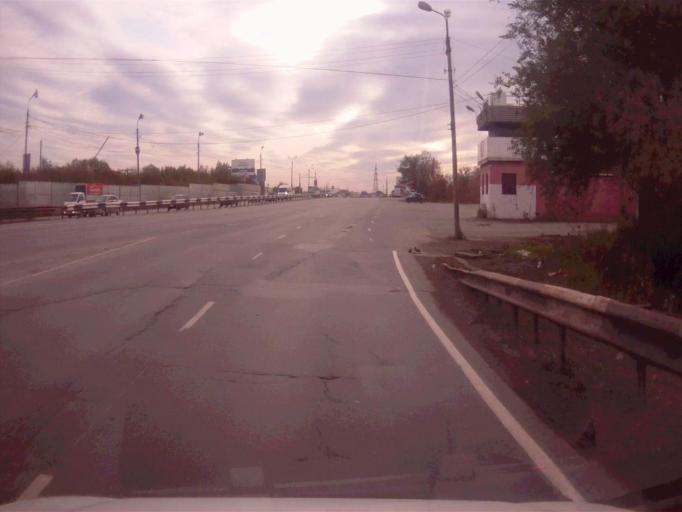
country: RU
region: Chelyabinsk
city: Novosineglazovskiy
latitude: 55.0775
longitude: 61.3883
